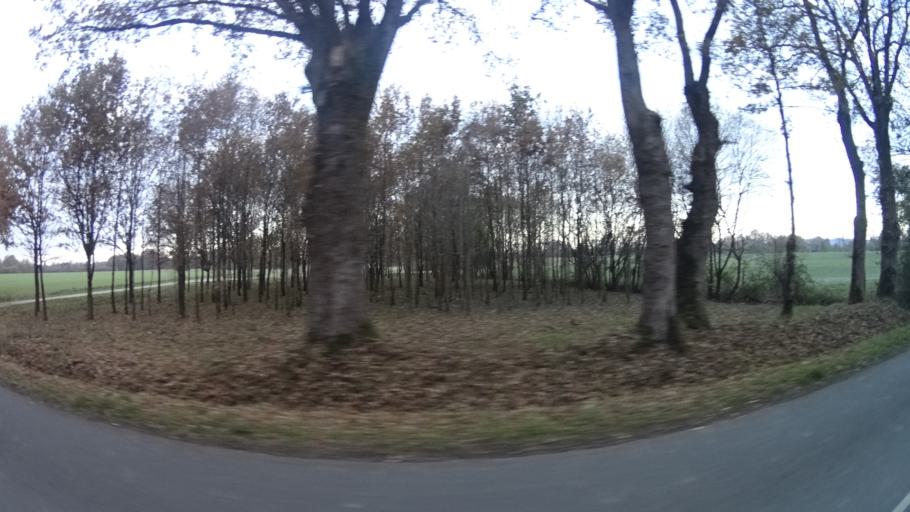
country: FR
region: Brittany
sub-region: Departement d'Ille-et-Vilaine
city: Langon
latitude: 47.6800
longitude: -1.8831
